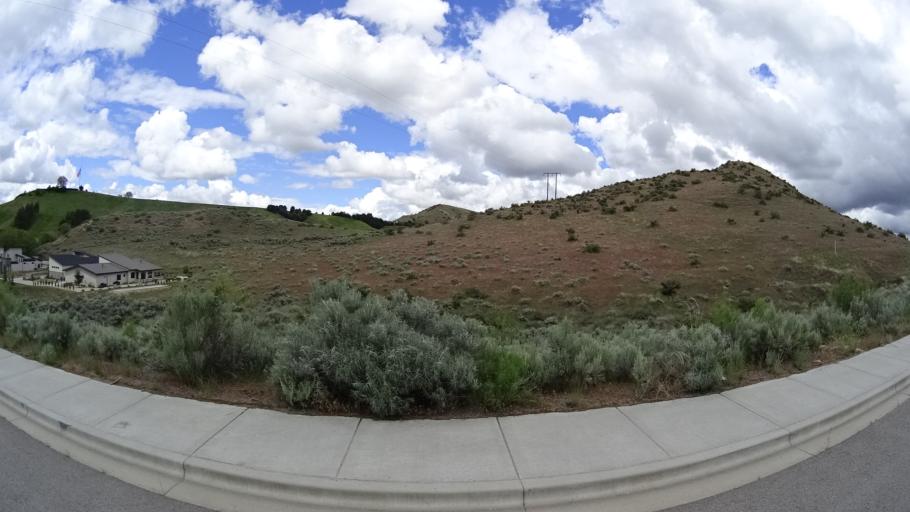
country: US
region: Idaho
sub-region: Ada County
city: Boise
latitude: 43.6539
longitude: -116.1908
